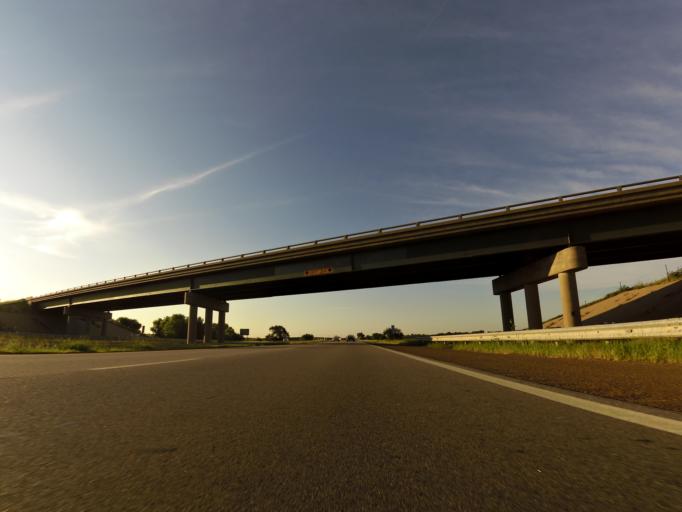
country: US
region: Kansas
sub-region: Sedgwick County
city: Maize
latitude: 37.7665
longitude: -97.4501
